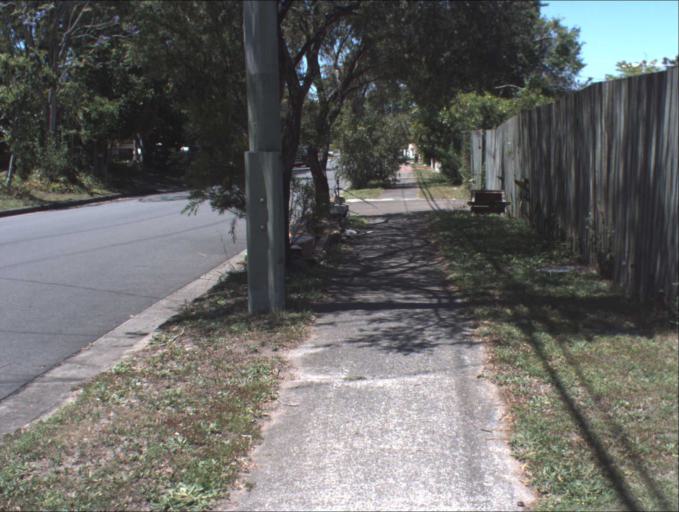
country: AU
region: Queensland
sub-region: Logan
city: Logan City
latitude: -27.6407
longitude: 153.1227
